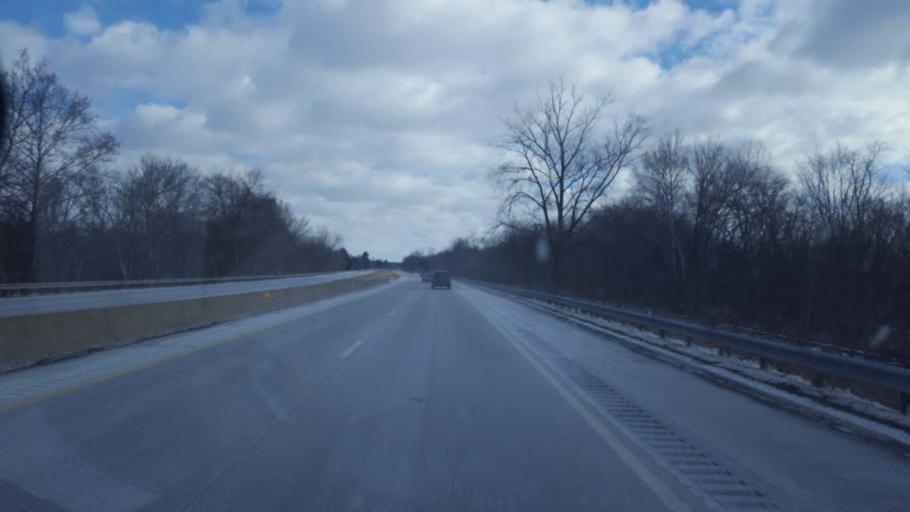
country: US
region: Ohio
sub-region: Licking County
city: Newark
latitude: 40.0641
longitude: -82.3220
